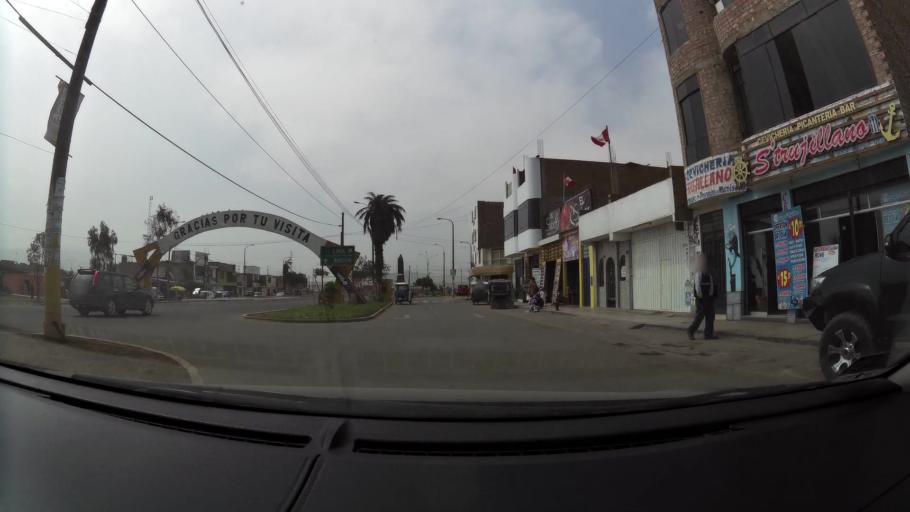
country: PE
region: Lima
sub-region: Lima
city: Santa Rosa
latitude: -11.7864
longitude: -77.1559
